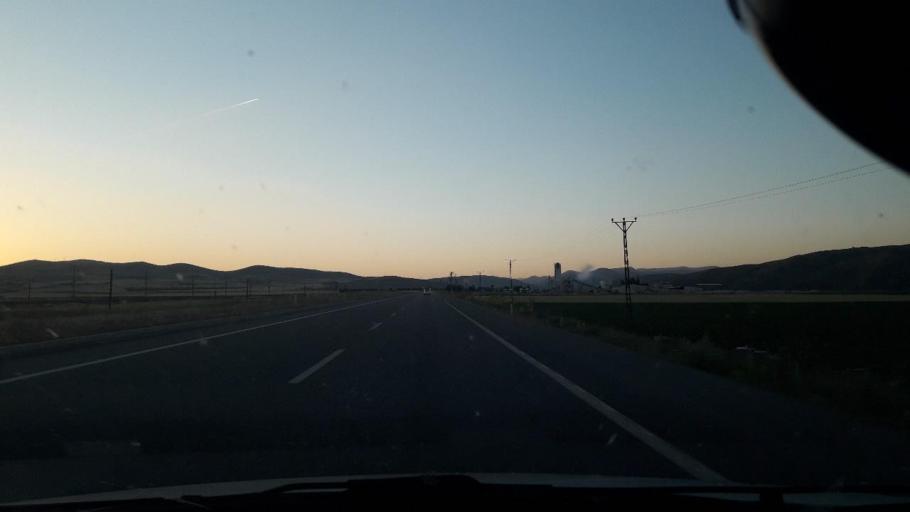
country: TR
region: Malatya
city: Yazihan
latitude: 38.6073
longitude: 38.1770
